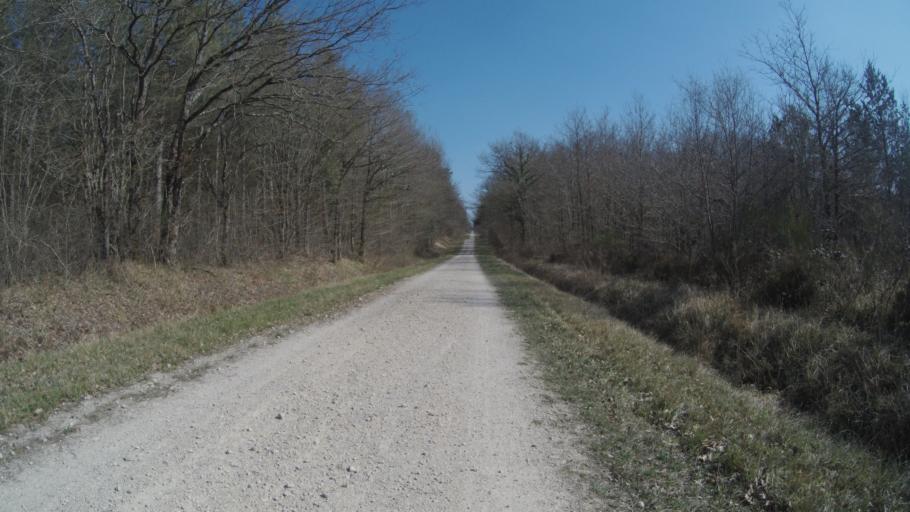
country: FR
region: Centre
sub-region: Departement du Loiret
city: Chanteau
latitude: 47.9507
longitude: 1.9596
